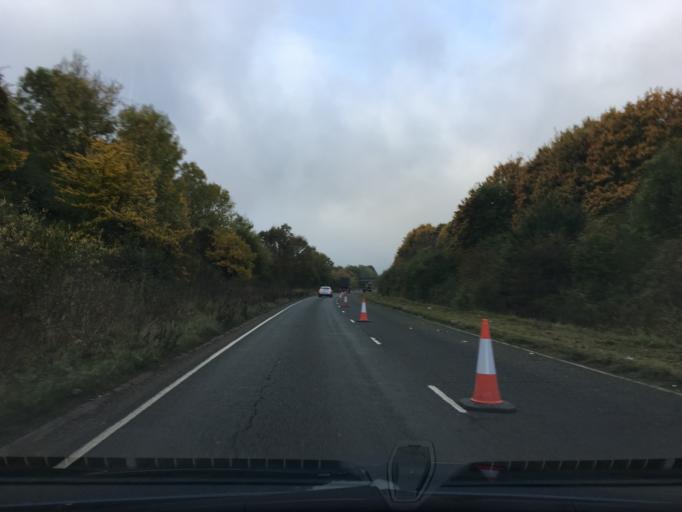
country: GB
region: England
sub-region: Hampshire
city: Alton
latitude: 51.1551
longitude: -0.9504
